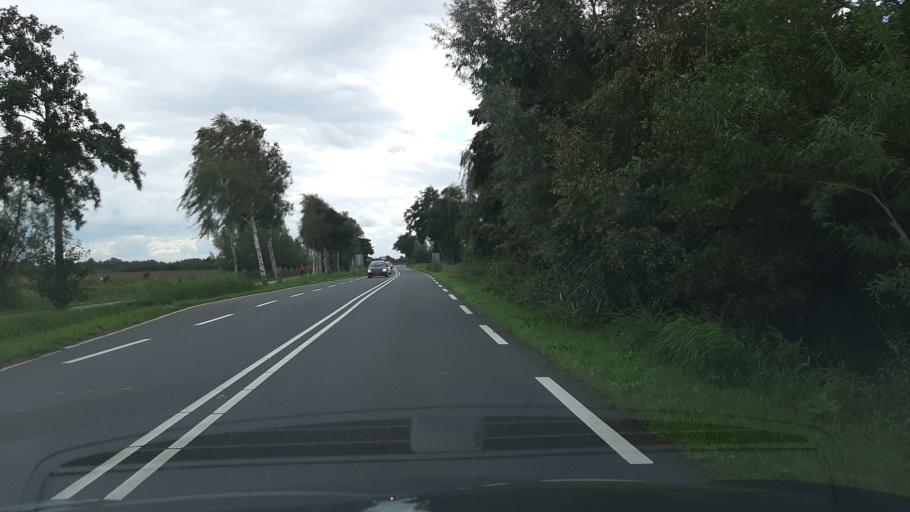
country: NL
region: Overijssel
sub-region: Gemeente Steenwijkerland
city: Giethoorn
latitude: 52.7059
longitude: 6.0733
